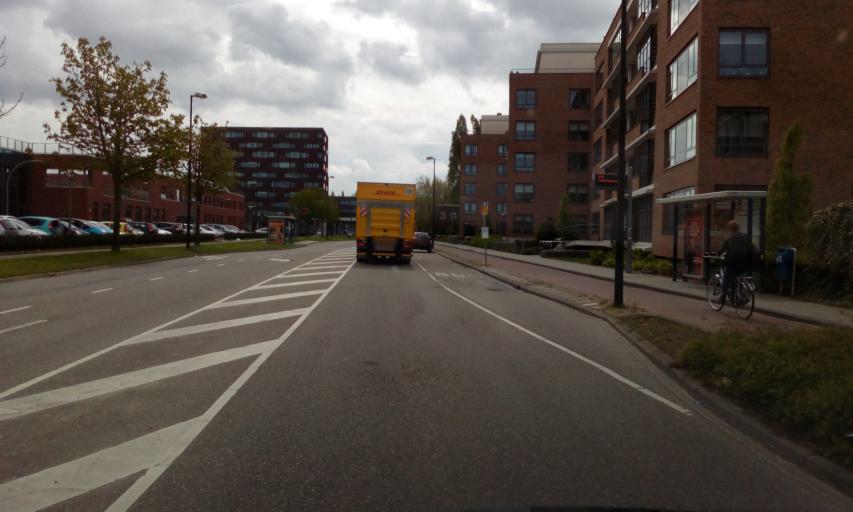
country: NL
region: South Holland
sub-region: Gemeente Vlaardingen
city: Vlaardingen
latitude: 51.9161
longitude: 4.3591
